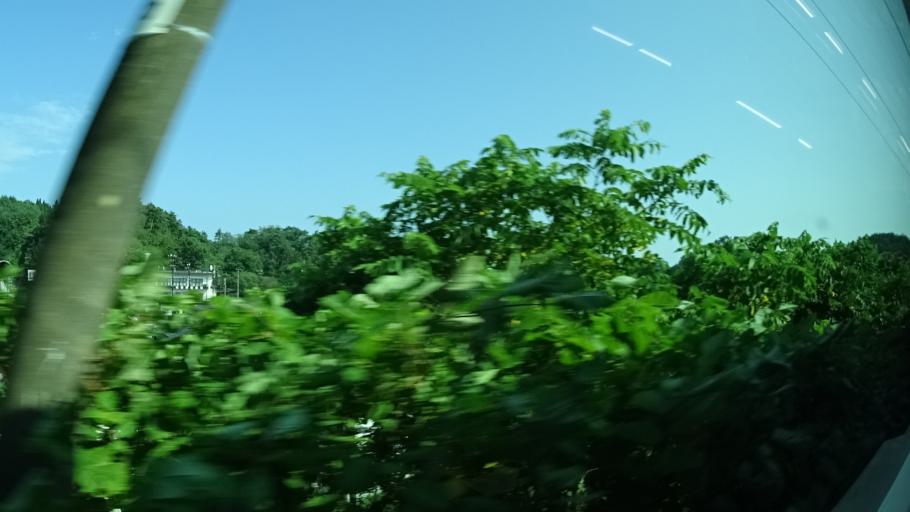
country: JP
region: Miyagi
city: Matsushima
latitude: 38.3520
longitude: 141.0422
